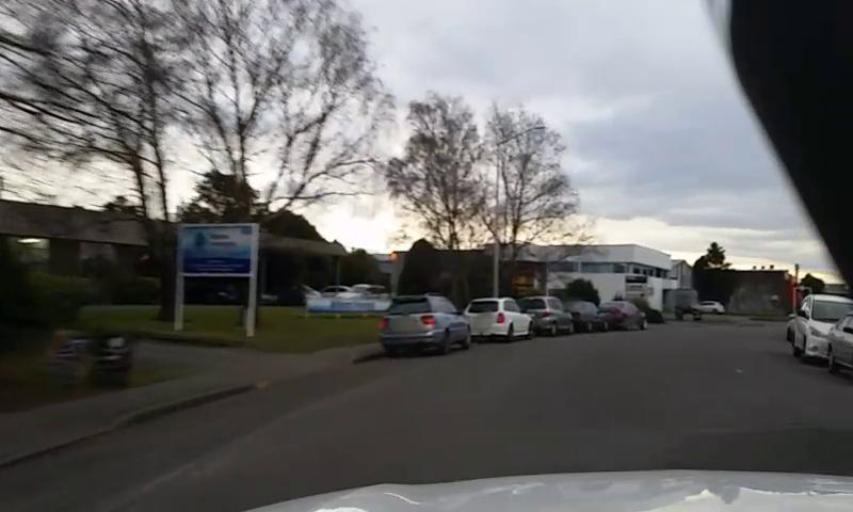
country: NZ
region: Canterbury
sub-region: Christchurch City
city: Christchurch
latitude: -43.4910
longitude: 172.5608
